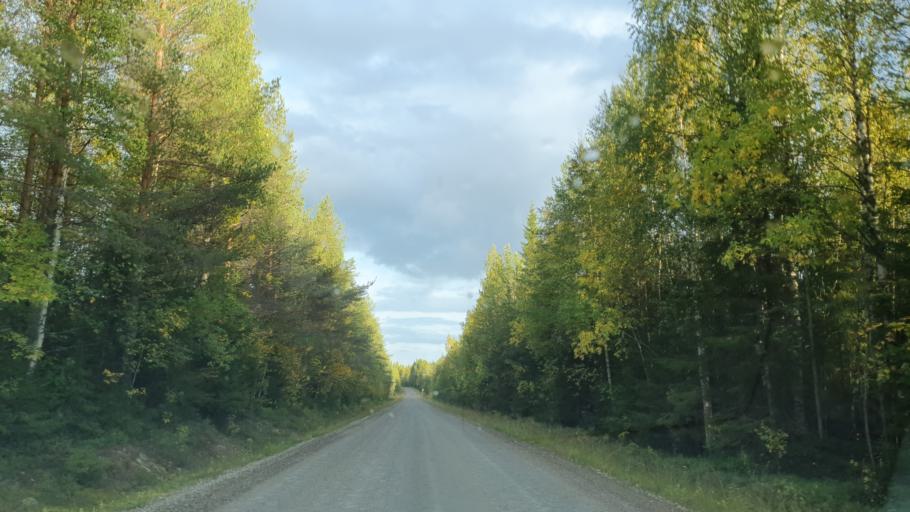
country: FI
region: Kainuu
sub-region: Kehys-Kainuu
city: Kuhmo
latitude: 64.4281
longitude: 29.3273
